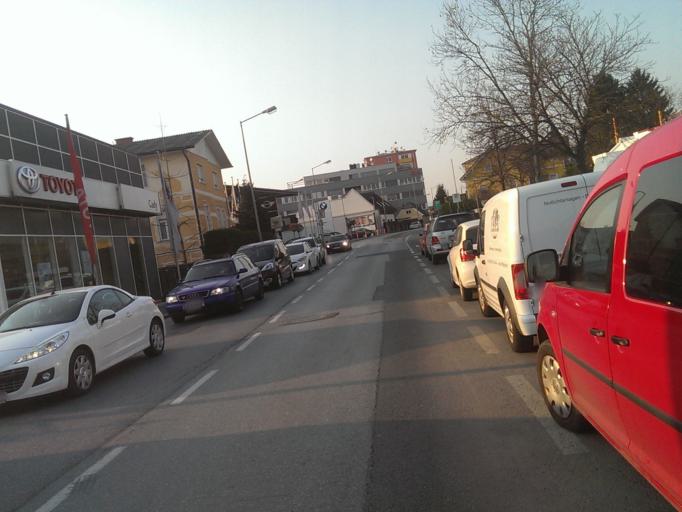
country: AT
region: Styria
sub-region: Graz Stadt
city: Graz
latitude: 47.0429
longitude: 15.4583
